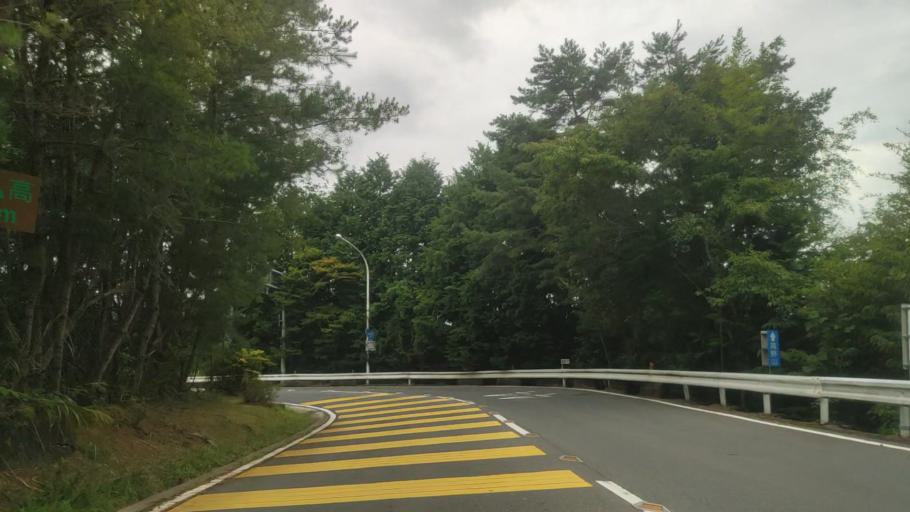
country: JP
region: Wakayama
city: Koya
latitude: 34.2189
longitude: 135.5369
